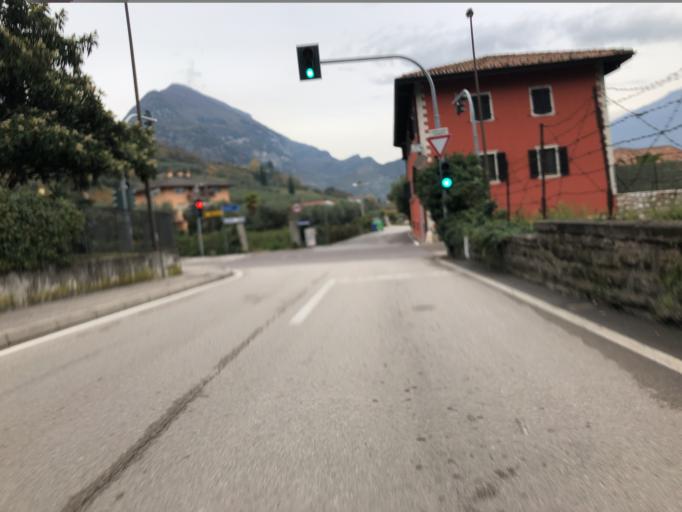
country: IT
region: Trentino-Alto Adige
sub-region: Provincia di Trento
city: Tenno
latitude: 45.9076
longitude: 10.8462
